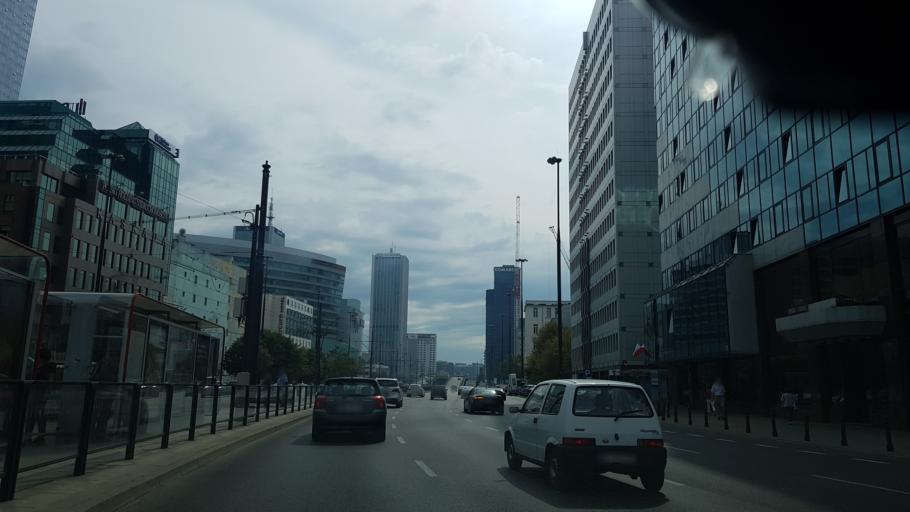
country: PL
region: Masovian Voivodeship
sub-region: Warszawa
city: Wola
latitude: 52.2324
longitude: 20.9987
